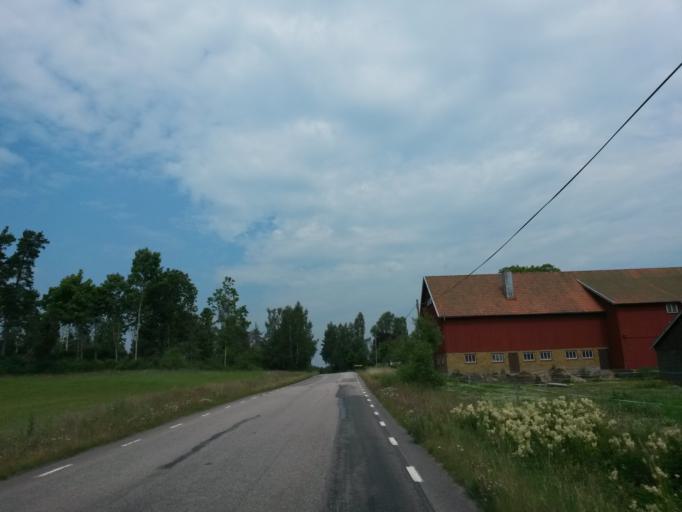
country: SE
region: Vaestra Goetaland
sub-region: Vargarda Kommun
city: Vargarda
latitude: 58.1210
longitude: 12.7874
